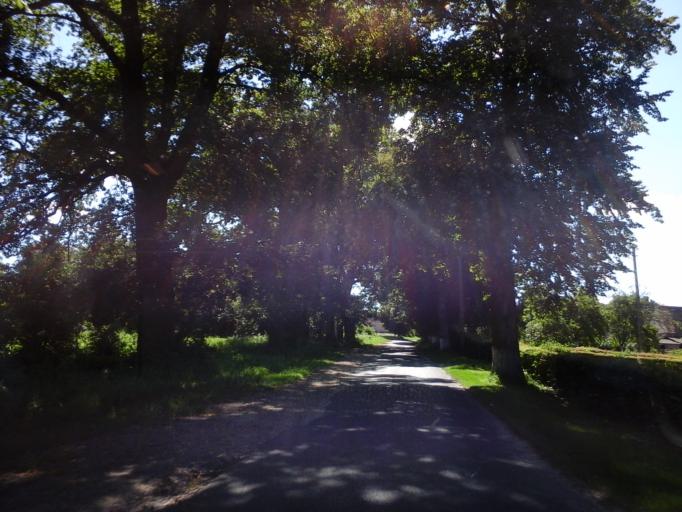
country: PL
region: West Pomeranian Voivodeship
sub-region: Powiat choszczenski
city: Recz
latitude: 53.2199
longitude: 15.4897
